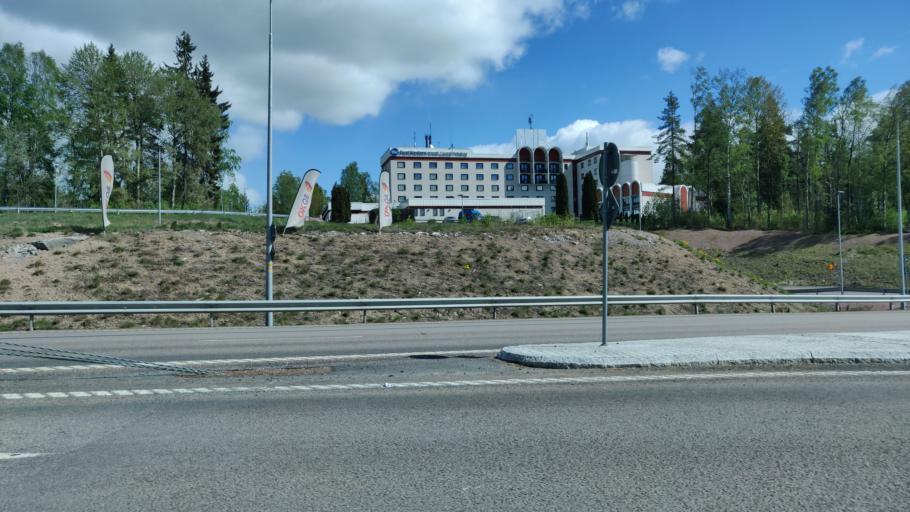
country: SE
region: Vaermland
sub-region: Karlstads Kommun
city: Karlstad
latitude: 59.4005
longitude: 13.5325
